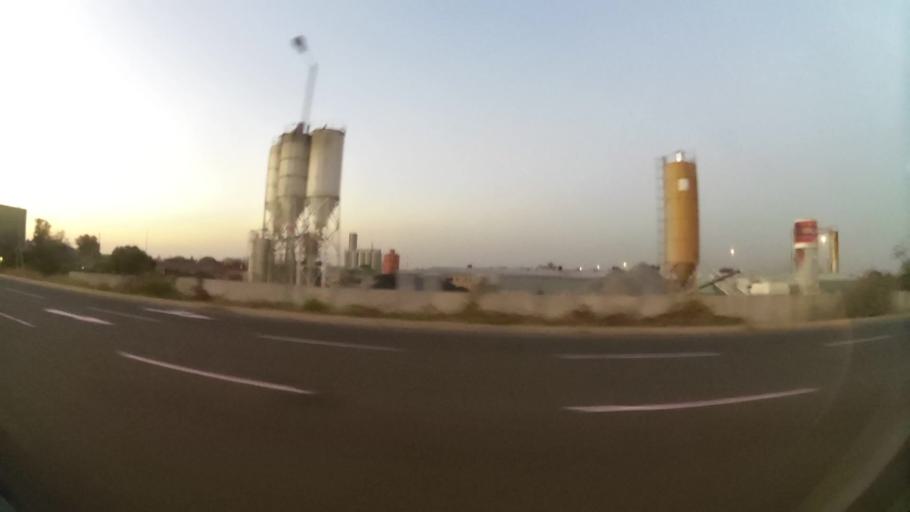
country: ZA
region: North-West
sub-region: Bojanala Platinum District Municipality
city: Rustenburg
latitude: -25.6810
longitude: 27.2548
